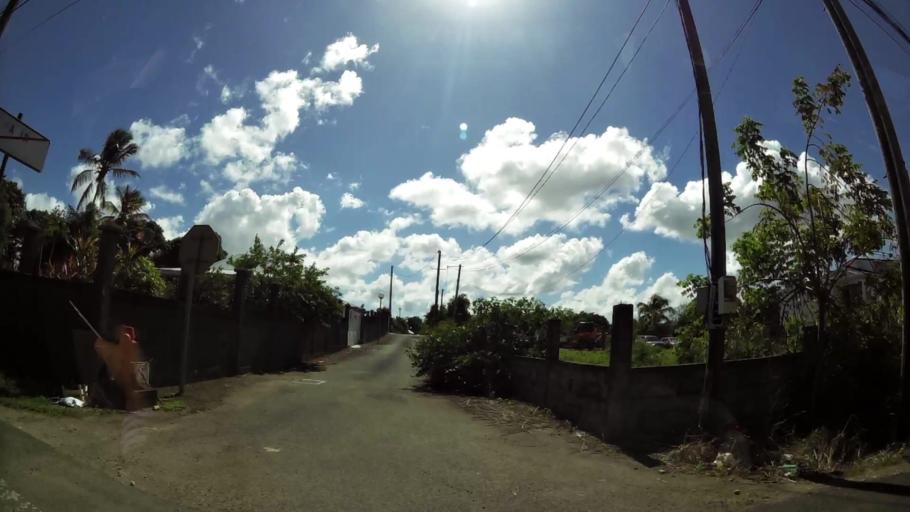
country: GP
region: Guadeloupe
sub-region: Guadeloupe
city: Petit-Canal
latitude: 16.3690
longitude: -61.4429
